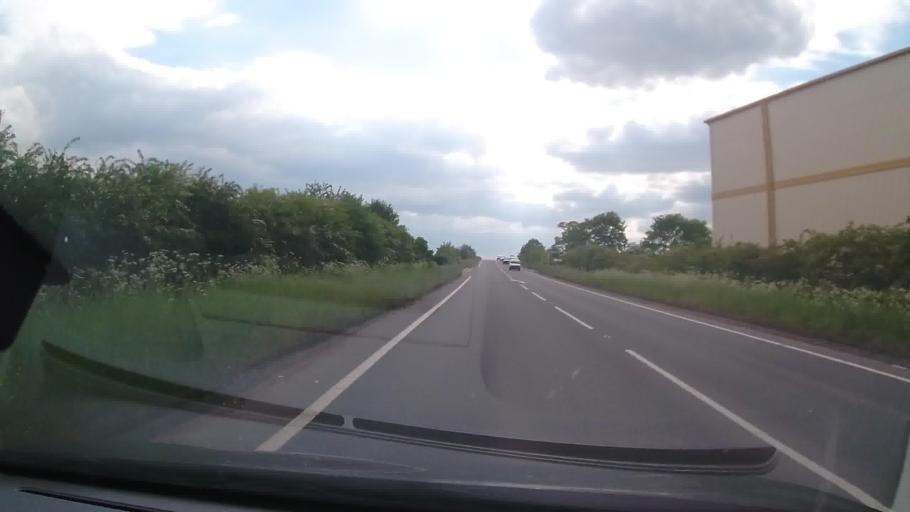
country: GB
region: England
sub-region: Shropshire
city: Whitchurch
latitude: 52.9621
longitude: -2.6666
